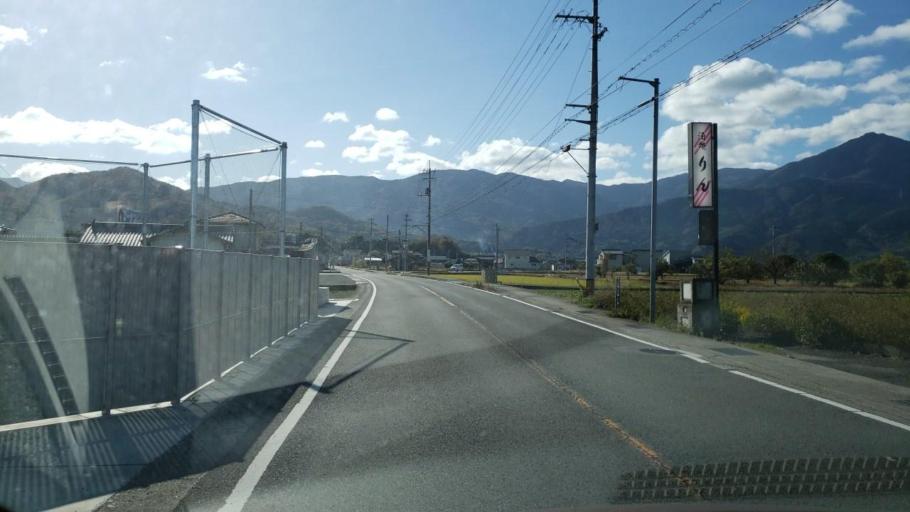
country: JP
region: Tokushima
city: Wakimachi
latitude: 34.0644
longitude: 134.2380
